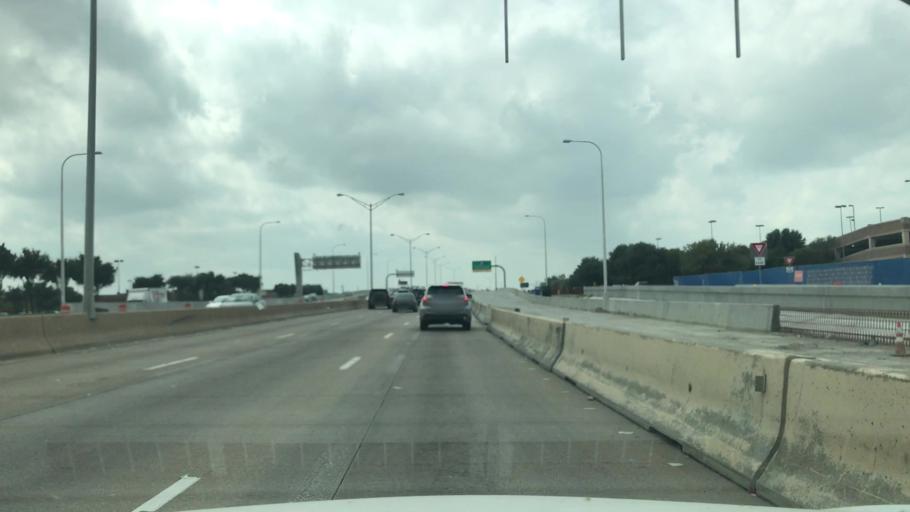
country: US
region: Texas
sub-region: Dallas County
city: Addison
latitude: 33.0319
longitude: -96.8293
